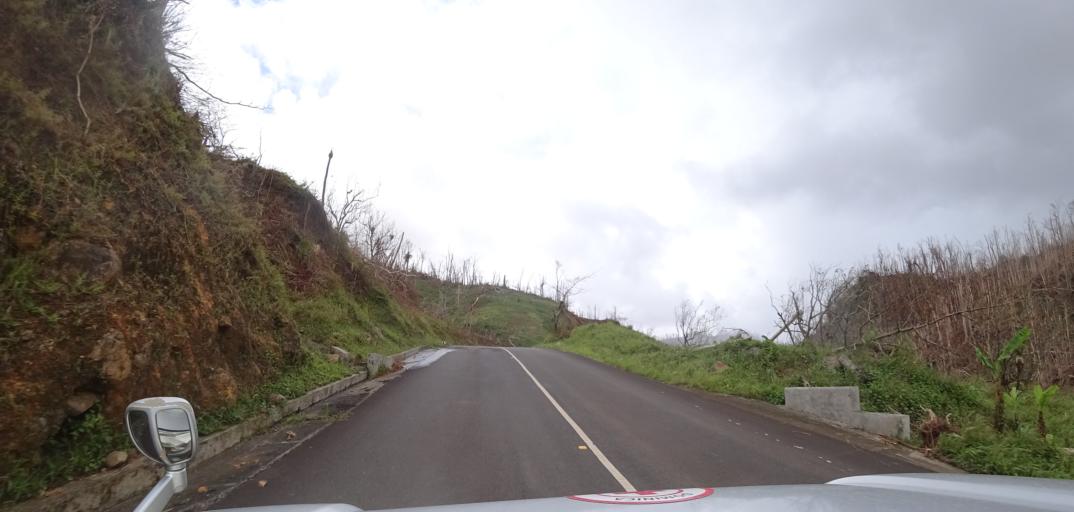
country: DM
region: Saint David
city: Castle Bruce
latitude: 15.4705
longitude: -61.3015
